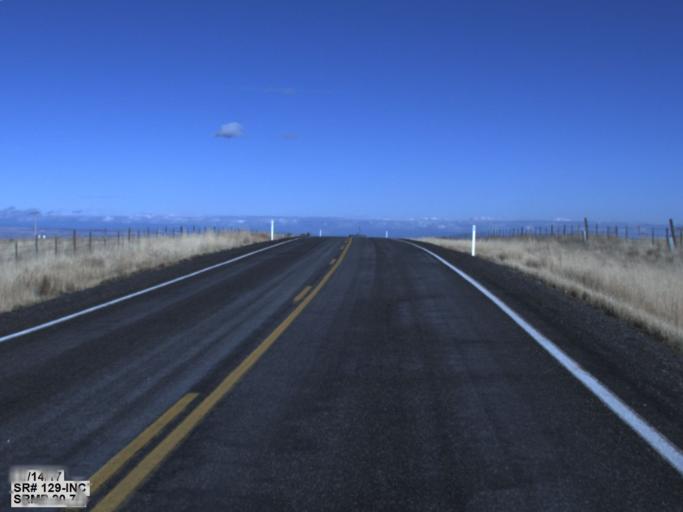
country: US
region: Washington
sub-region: Asotin County
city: Asotin
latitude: 46.1686
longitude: -117.0877
